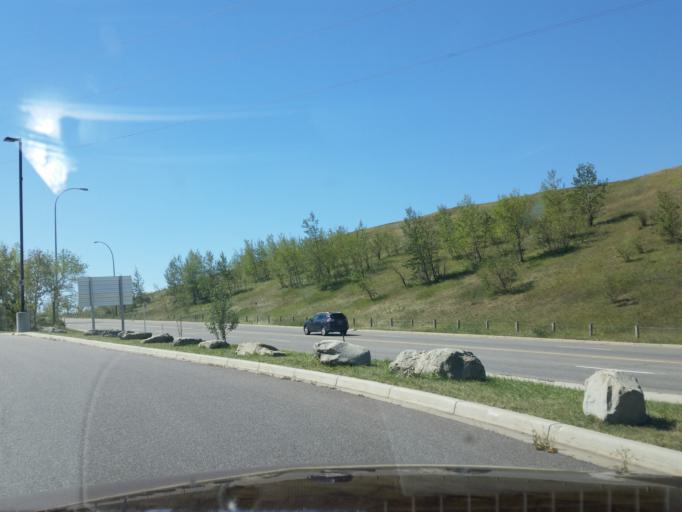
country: CA
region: Alberta
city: Calgary
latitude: 51.0507
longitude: -114.0255
